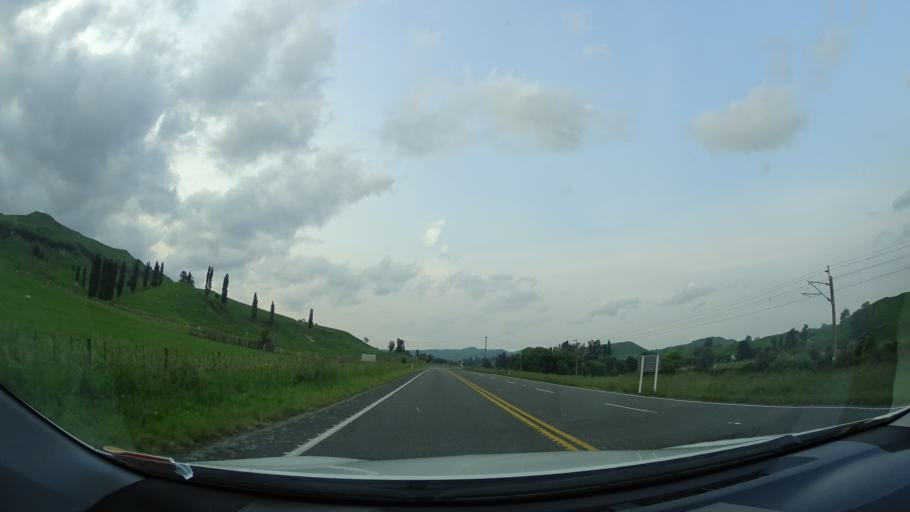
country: NZ
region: Manawatu-Wanganui
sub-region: Ruapehu District
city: Waiouru
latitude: -39.7222
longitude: 175.8411
